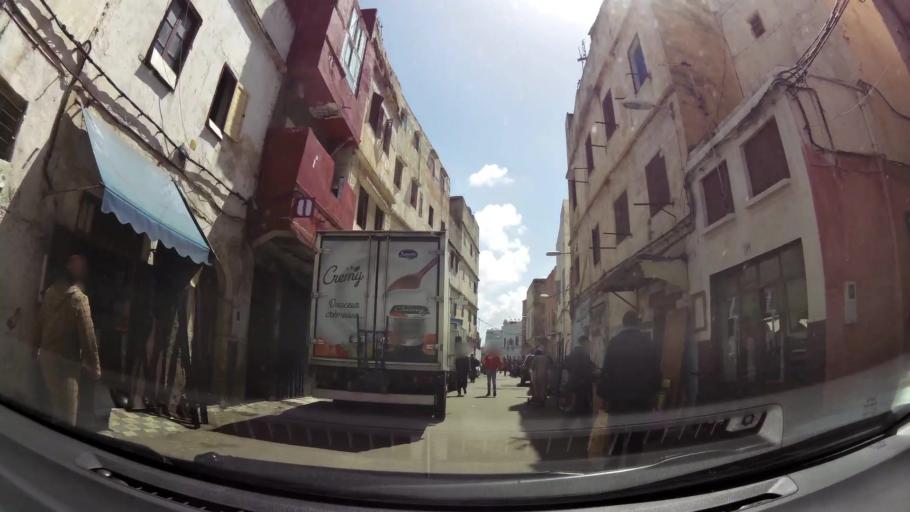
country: MA
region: Grand Casablanca
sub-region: Casablanca
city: Casablanca
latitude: 33.5997
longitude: -7.6254
